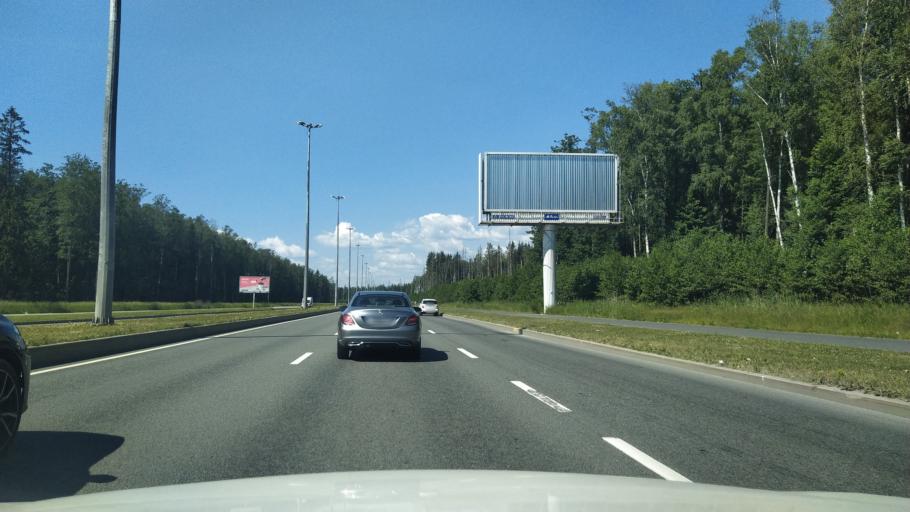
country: RU
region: Leningrad
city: Untolovo
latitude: 60.0568
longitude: 30.2225
